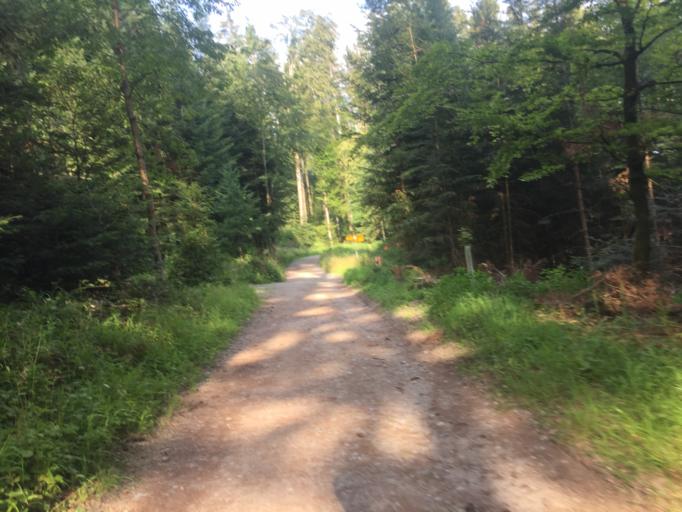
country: CH
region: Bern
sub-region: Bern-Mittelland District
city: Stettlen
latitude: 46.9380
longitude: 7.5310
